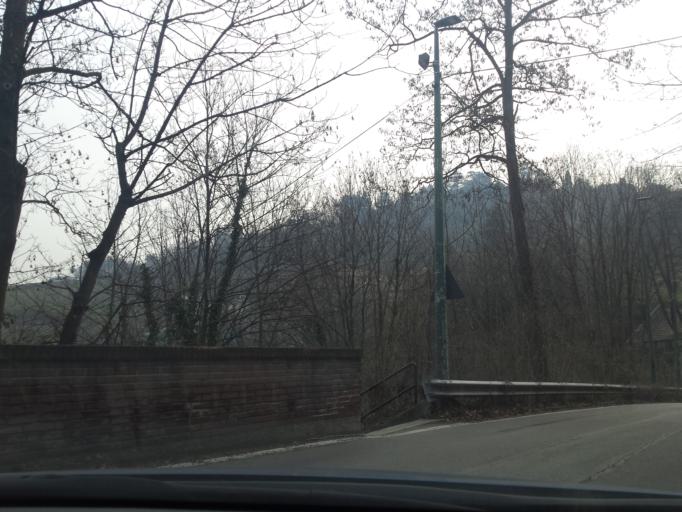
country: IT
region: Piedmont
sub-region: Provincia di Torino
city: Turin
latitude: 45.0580
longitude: 7.7060
